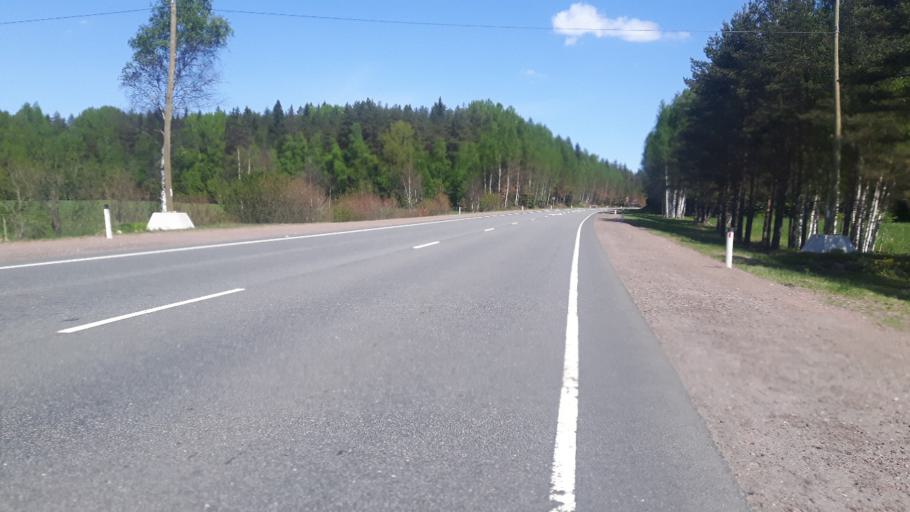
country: RU
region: Leningrad
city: Vysotsk
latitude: 60.6344
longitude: 28.2756
